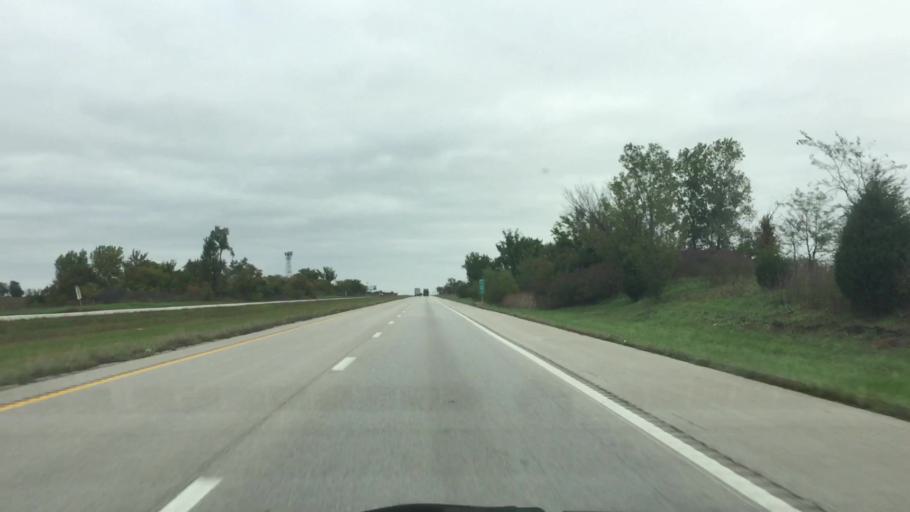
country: US
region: Missouri
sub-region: Clinton County
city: Cameron
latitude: 39.8241
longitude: -94.1896
